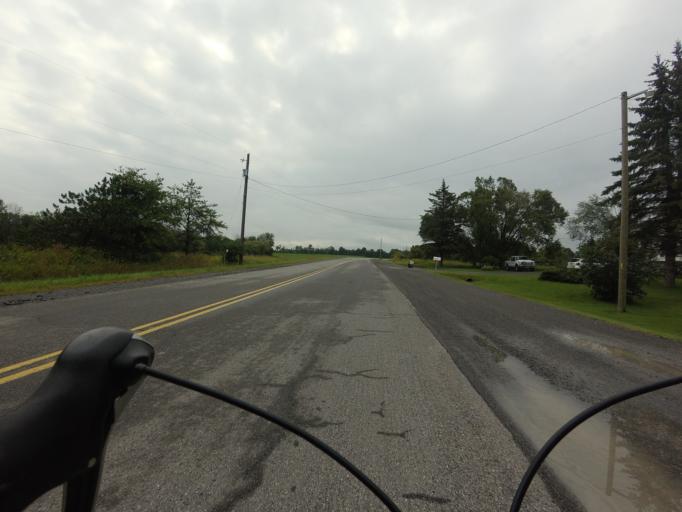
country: CA
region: Ontario
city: Bells Corners
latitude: 45.1731
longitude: -75.8140
